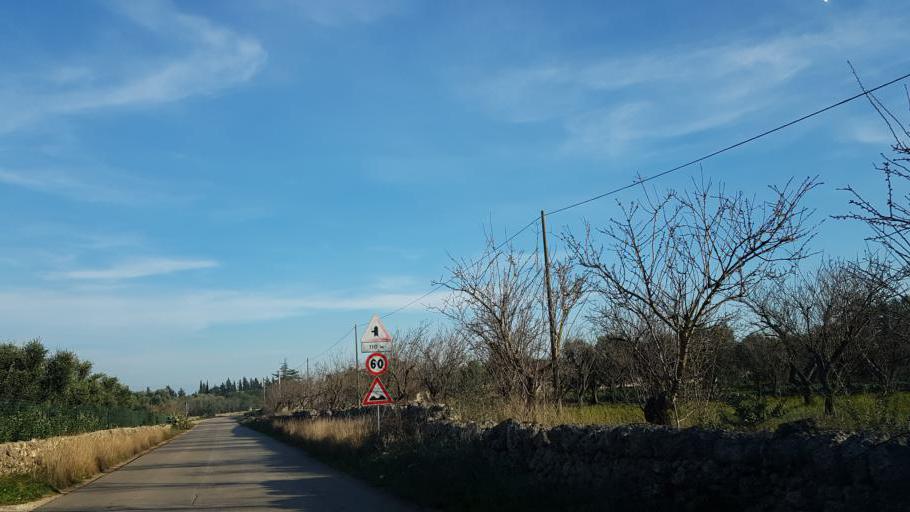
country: IT
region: Apulia
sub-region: Provincia di Brindisi
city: San Vito dei Normanni
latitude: 40.7001
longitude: 17.7340
